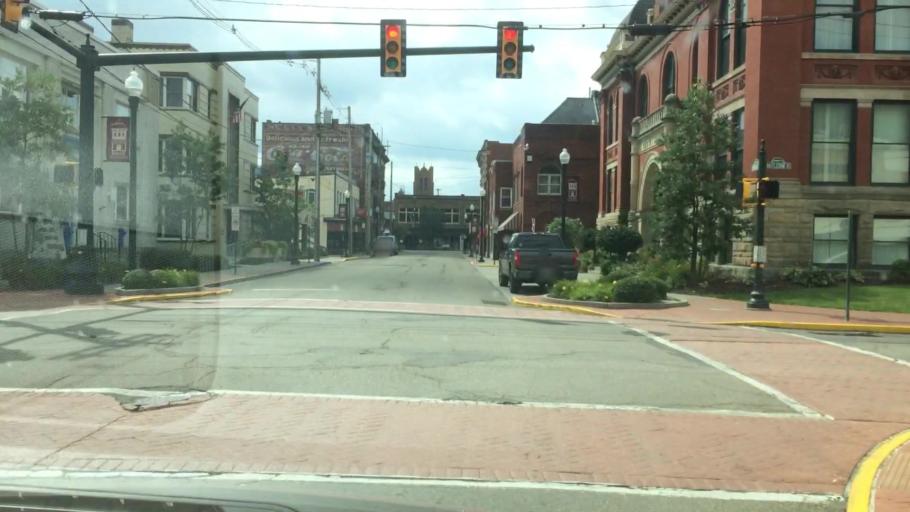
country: US
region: Pennsylvania
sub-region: McKean County
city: Bradford
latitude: 41.9575
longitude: -78.6475
